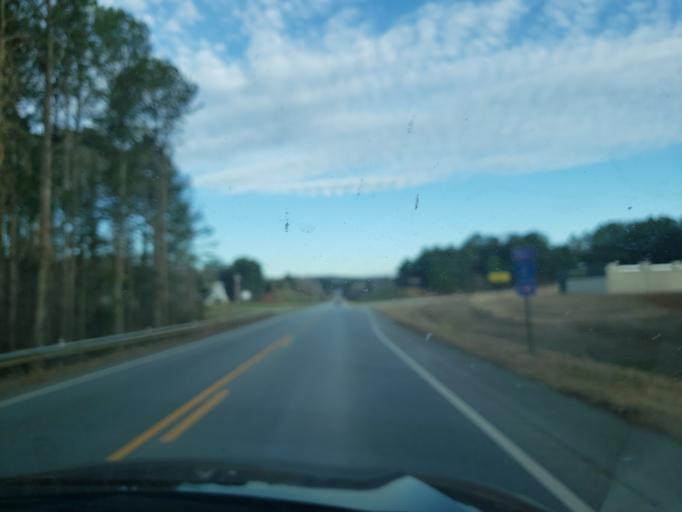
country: US
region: Alabama
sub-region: Randolph County
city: Wedowee
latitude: 33.3773
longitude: -85.5119
